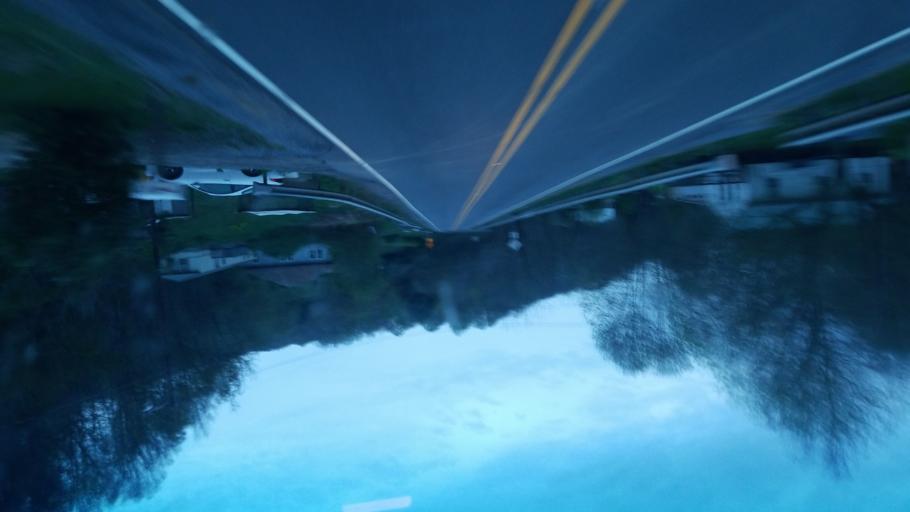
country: US
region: Virginia
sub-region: Smyth County
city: Atkins
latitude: 36.8172
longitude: -81.4492
